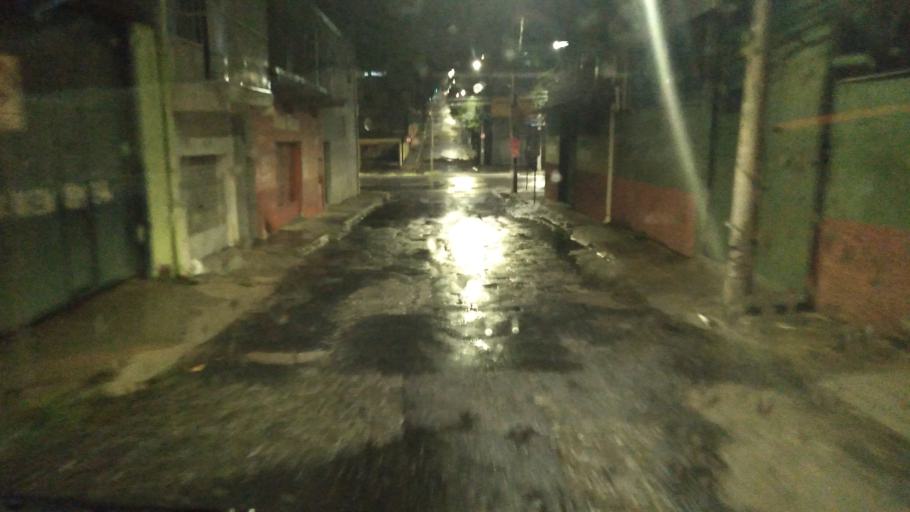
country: BR
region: Minas Gerais
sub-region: Belo Horizonte
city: Belo Horizonte
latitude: -19.9120
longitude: -43.9786
